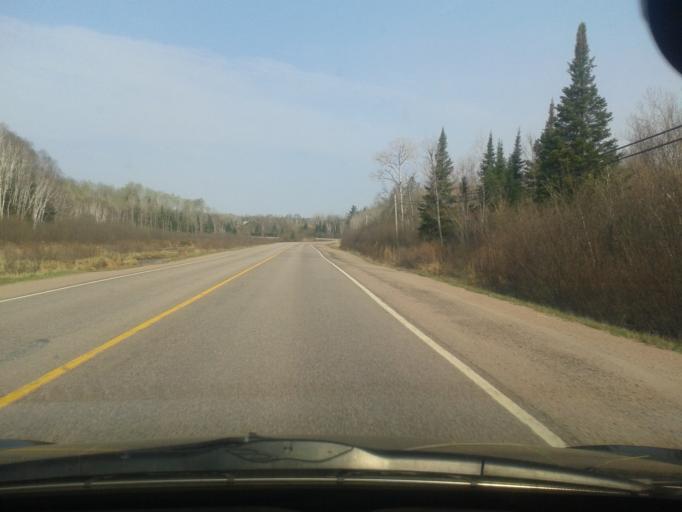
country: CA
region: Ontario
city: Powassan
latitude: 46.1923
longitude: -79.3175
